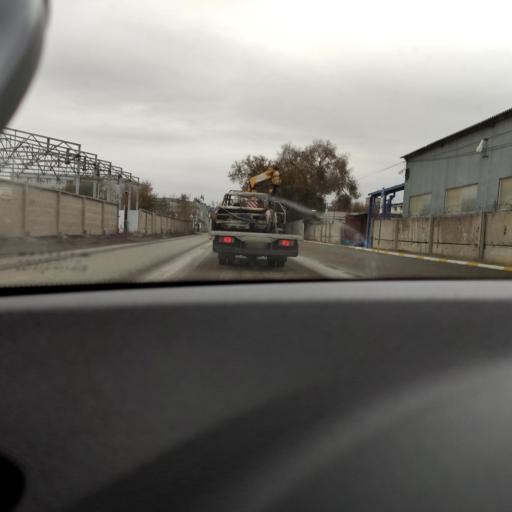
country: RU
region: Samara
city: Smyshlyayevka
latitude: 53.2078
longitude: 50.3022
